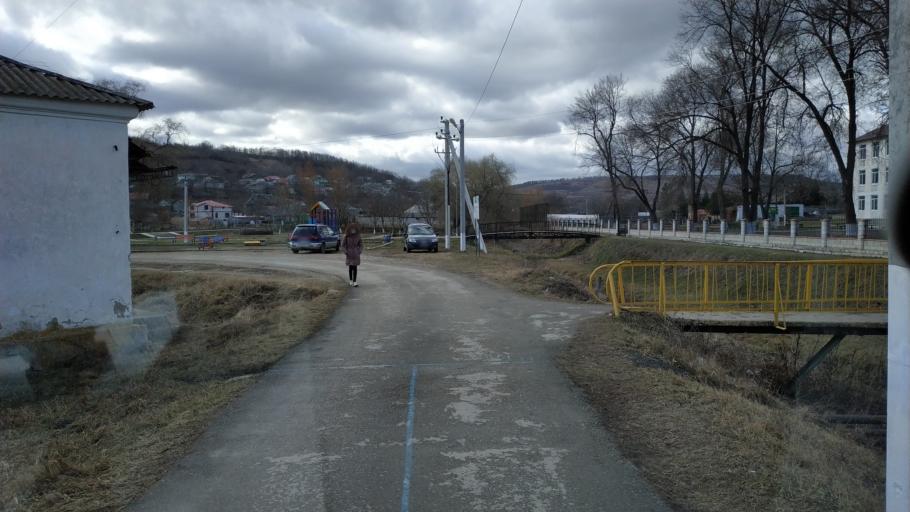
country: MD
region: Stinga Nistrului
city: Bucovat
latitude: 47.1355
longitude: 28.3830
